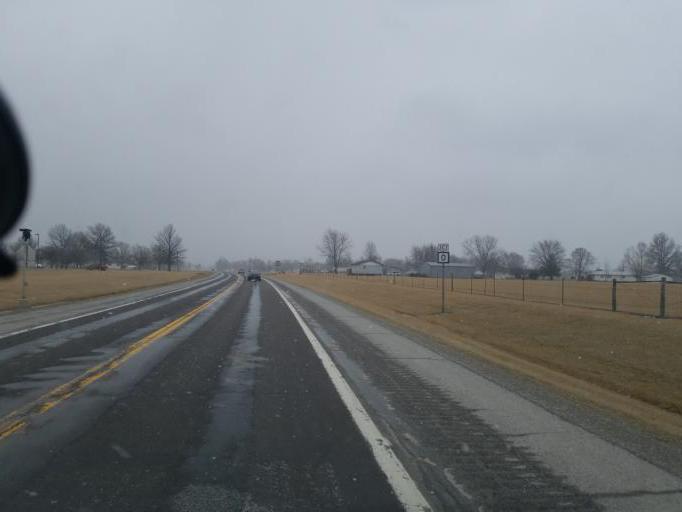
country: US
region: Missouri
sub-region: Schuyler County
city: Lancaster
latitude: 40.4197
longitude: -92.5676
